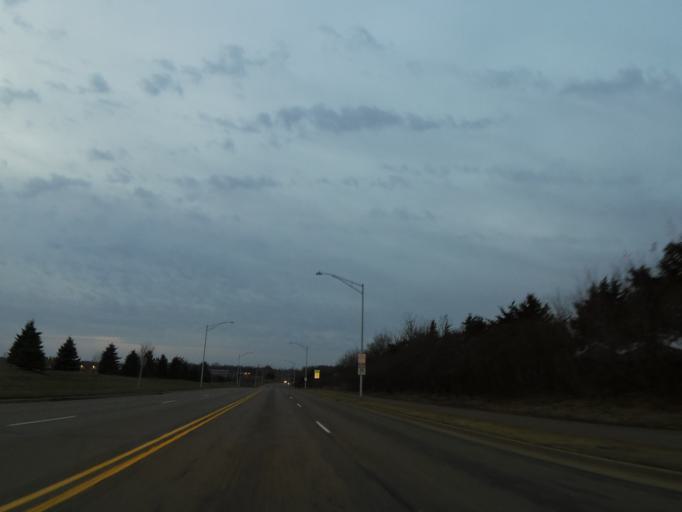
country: US
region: Wisconsin
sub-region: Saint Croix County
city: Hudson
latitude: 44.9490
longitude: -92.7026
